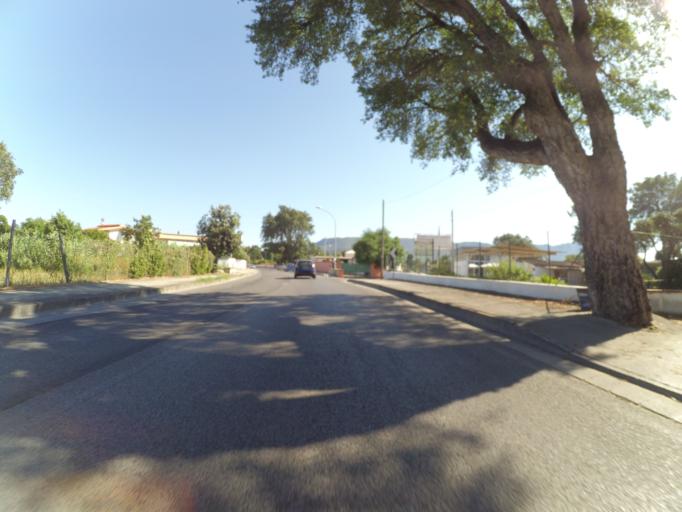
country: IT
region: Latium
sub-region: Provincia di Latina
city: San Felice Circeo
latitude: 41.2592
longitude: 13.0914
